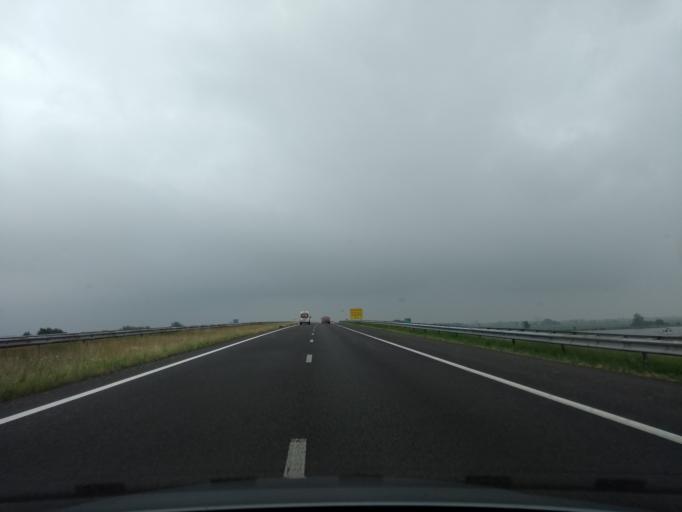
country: NL
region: Friesland
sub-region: Gemeente Skarsterlan
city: Joure
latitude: 52.9760
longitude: 5.7521
